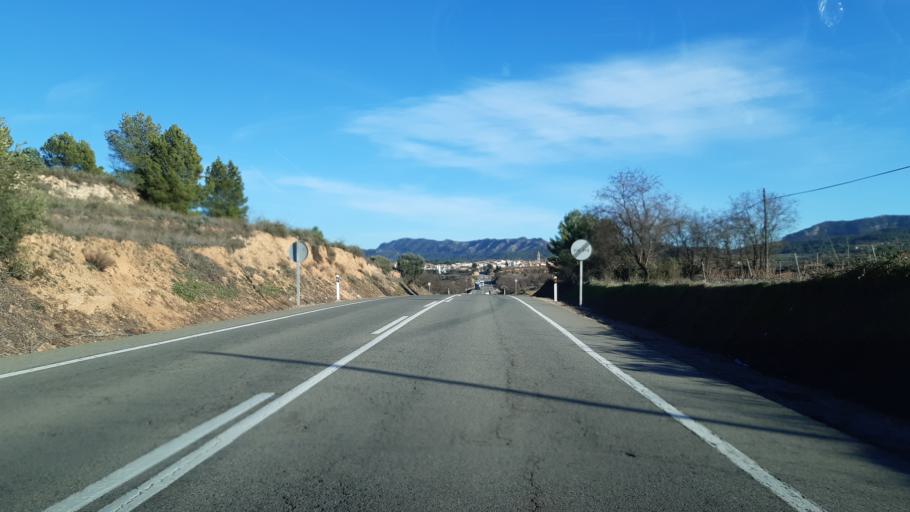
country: ES
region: Catalonia
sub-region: Provincia de Tarragona
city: Gandesa
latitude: 41.0545
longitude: 0.4164
